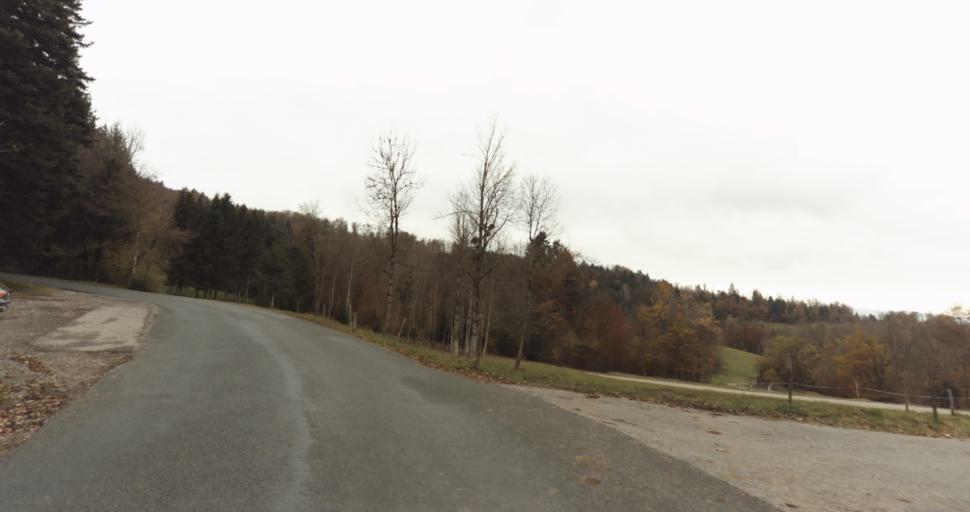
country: FR
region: Rhone-Alpes
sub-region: Departement de la Haute-Savoie
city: Saint-Martin-Bellevue
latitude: 45.9573
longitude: 6.1561
